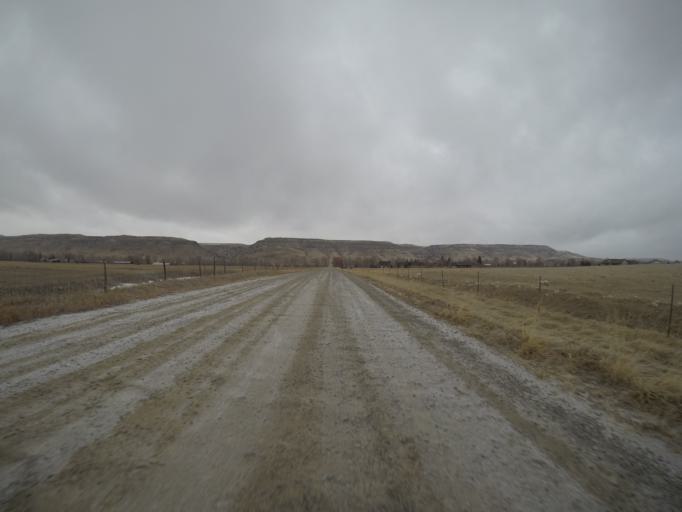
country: US
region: Montana
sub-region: Stillwater County
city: Absarokee
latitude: 45.5236
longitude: -109.4694
